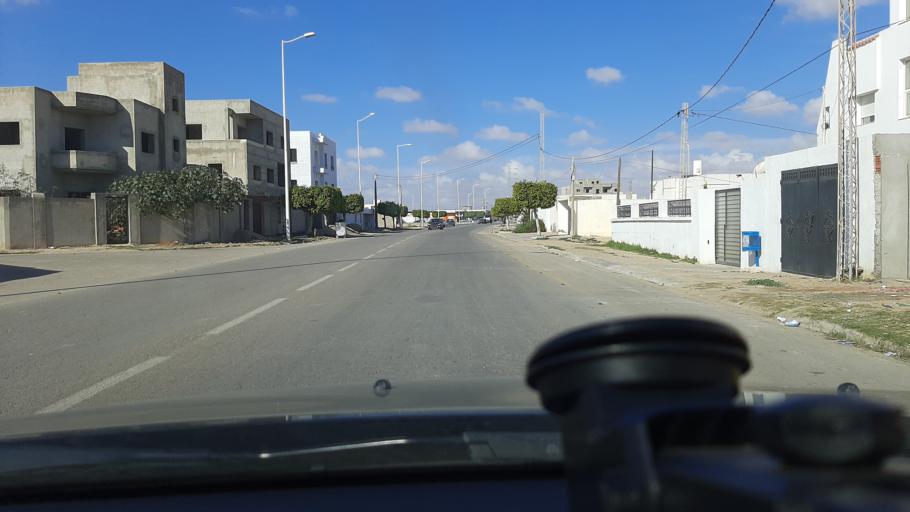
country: TN
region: Safaqis
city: Sfax
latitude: 34.8094
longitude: 10.7114
